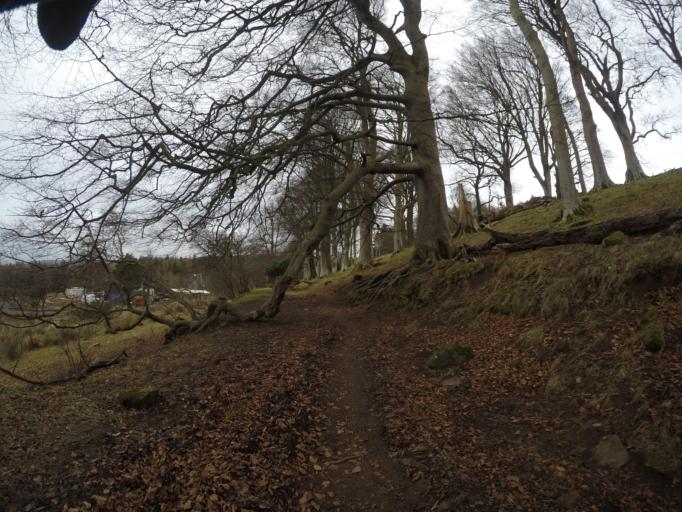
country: GB
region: Scotland
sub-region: North Ayrshire
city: Fairlie
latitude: 55.7606
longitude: -4.8495
